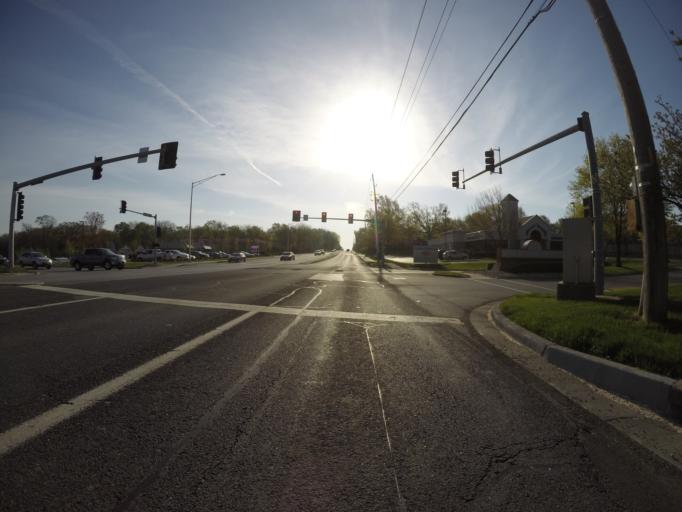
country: US
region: Missouri
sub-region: Jackson County
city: Lees Summit
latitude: 38.9174
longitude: -94.3594
